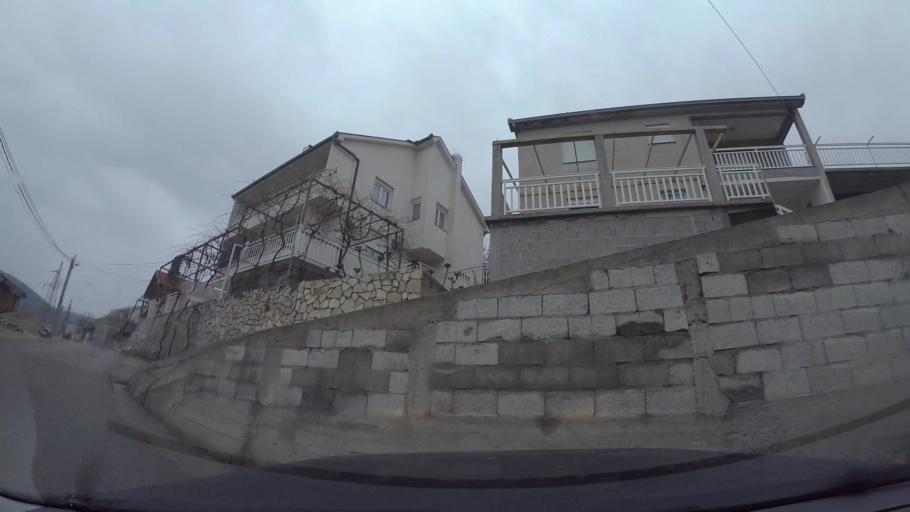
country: BA
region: Federation of Bosnia and Herzegovina
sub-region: Hercegovacko-Bosanski Kanton
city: Mostar
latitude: 43.3514
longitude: 17.8177
